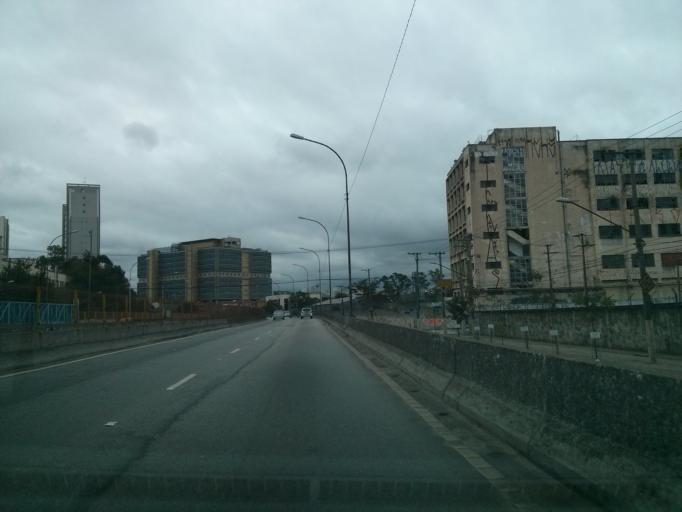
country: BR
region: Sao Paulo
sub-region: Sao Paulo
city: Sao Paulo
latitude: -23.5614
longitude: -46.6125
